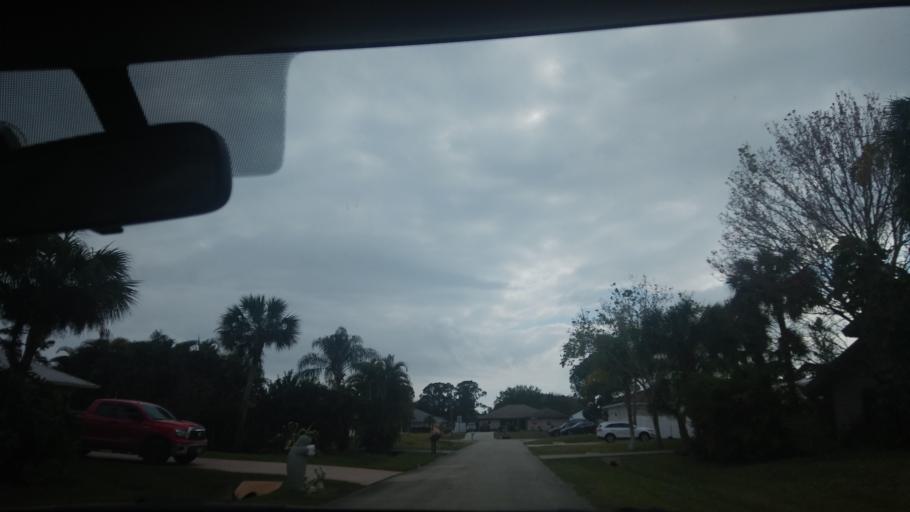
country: US
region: Florida
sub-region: Indian River County
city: Sebastian
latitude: 27.7989
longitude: -80.4875
